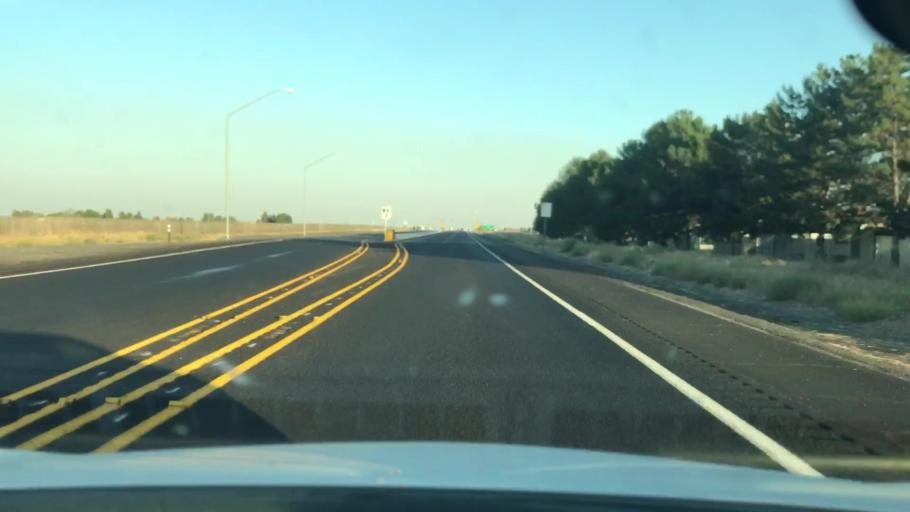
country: US
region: Washington
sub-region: Grant County
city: Cascade Valley
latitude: 47.1589
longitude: -119.3178
